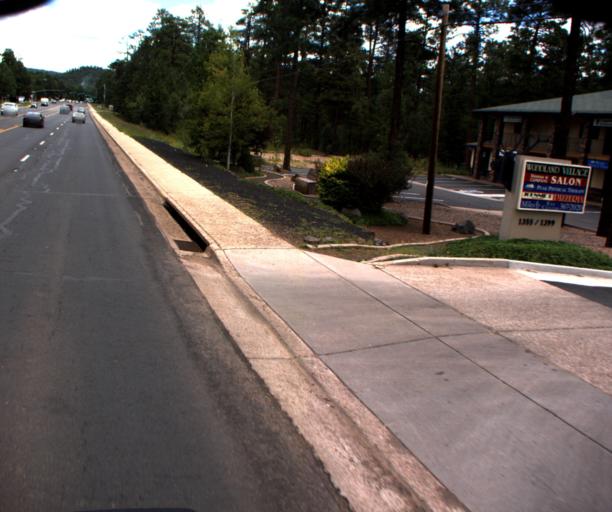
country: US
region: Arizona
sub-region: Navajo County
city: Pinetop-Lakeside
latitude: 34.1475
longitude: -109.9697
